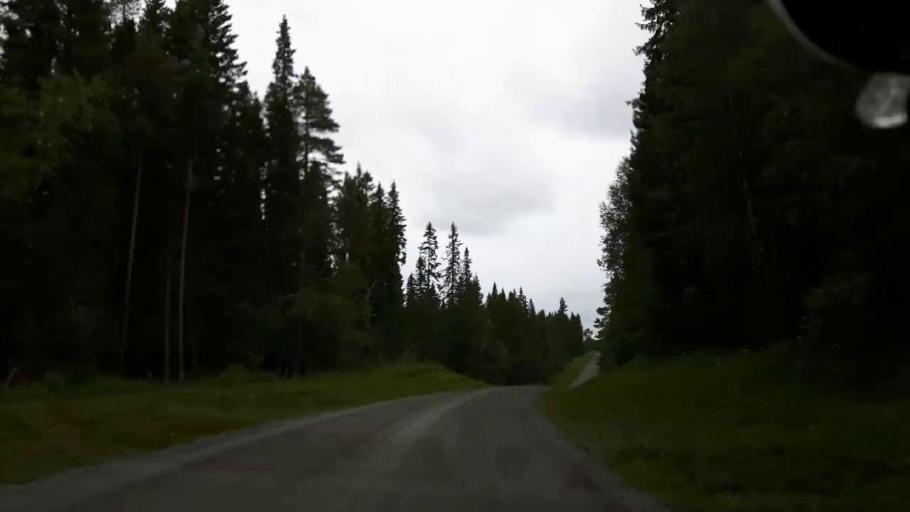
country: SE
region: Jaemtland
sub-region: OEstersunds Kommun
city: Ostersund
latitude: 63.0975
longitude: 14.5457
